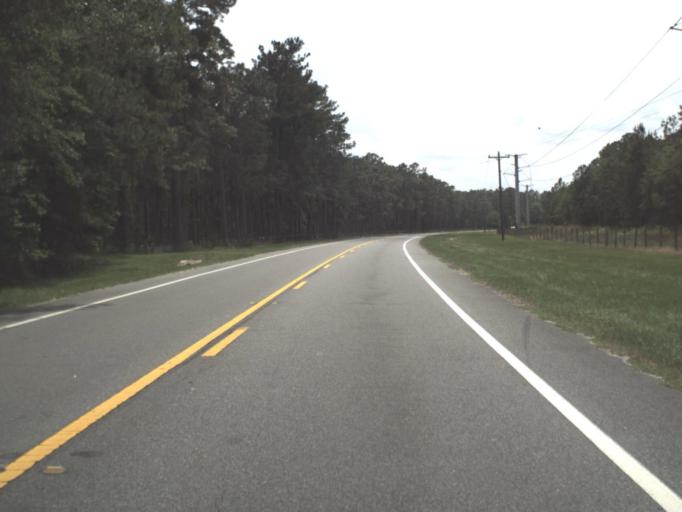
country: US
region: Florida
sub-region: Clay County
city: Asbury Lake
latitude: 29.9052
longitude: -81.8977
